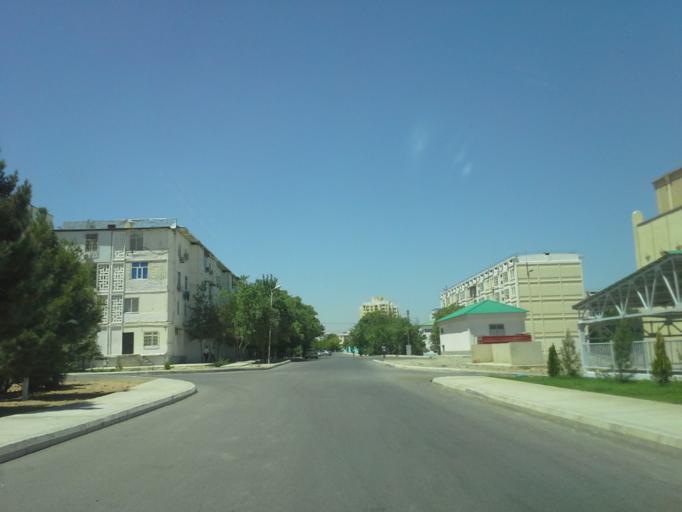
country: TM
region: Ahal
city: Ashgabat
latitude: 37.9131
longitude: 58.3969
